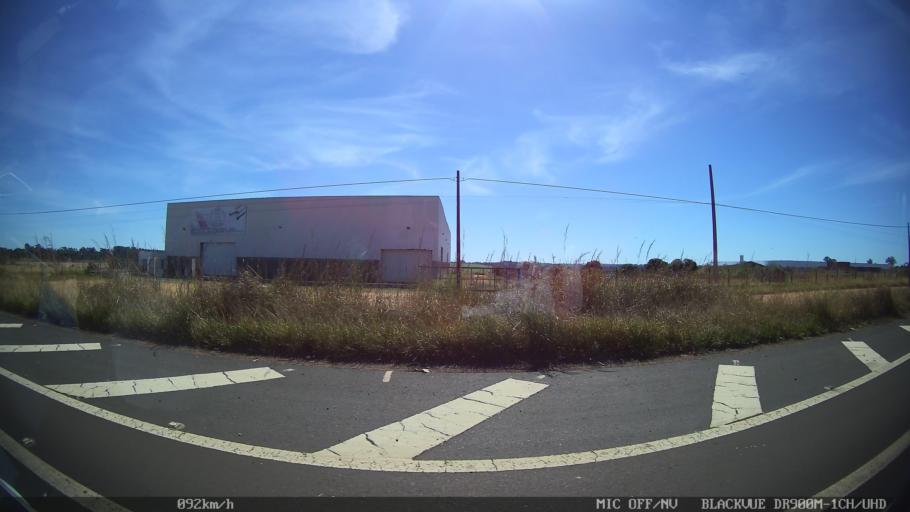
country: BR
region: Sao Paulo
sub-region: Franca
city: Franca
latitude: -20.5459
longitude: -47.4738
